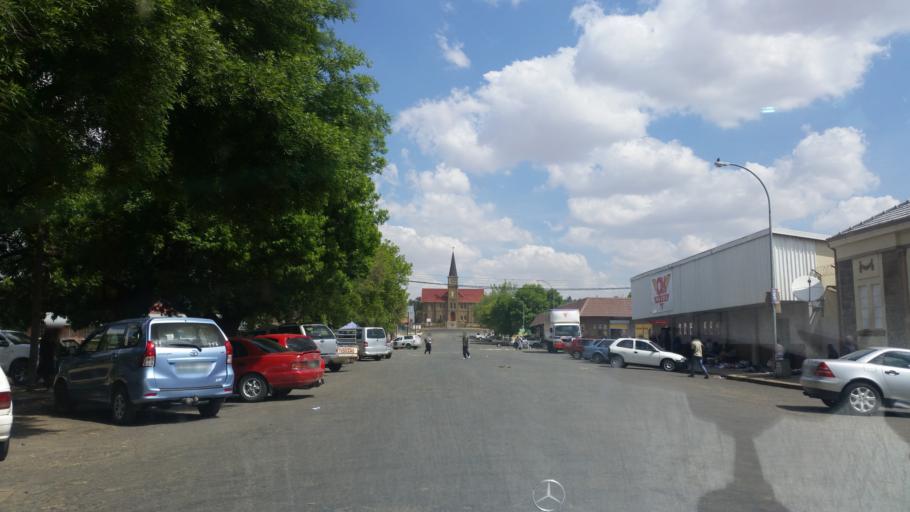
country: ZA
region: Orange Free State
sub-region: Thabo Mofutsanyana District Municipality
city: Reitz
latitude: -27.8017
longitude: 28.4306
